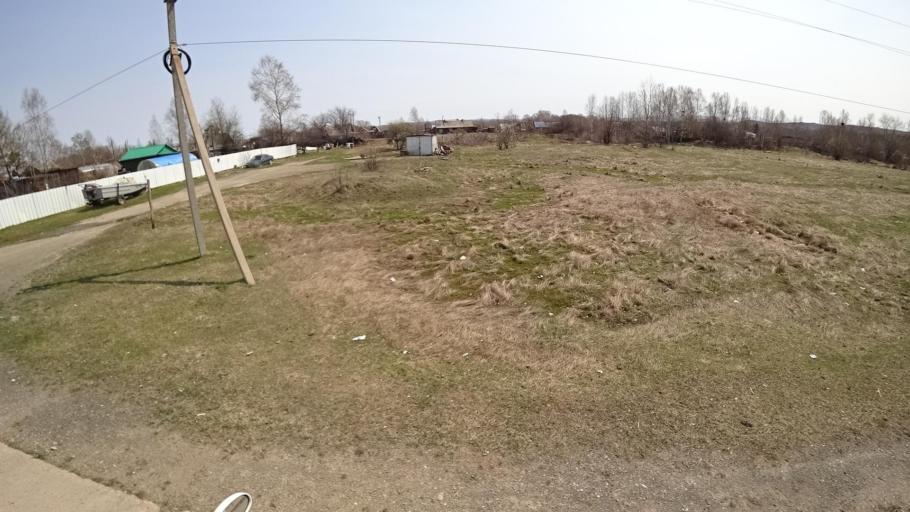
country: RU
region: Khabarovsk Krai
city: Selikhino
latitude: 50.3871
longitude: 137.3734
